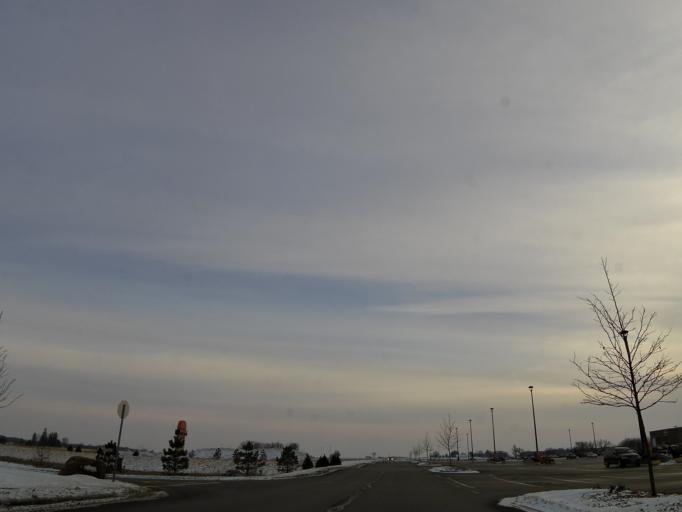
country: US
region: Minnesota
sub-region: Carver County
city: Carver
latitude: 44.7804
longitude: -93.6496
